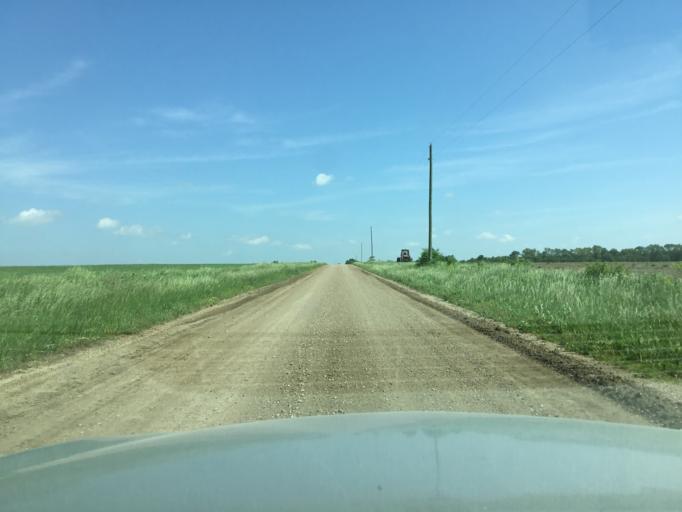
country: US
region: Kansas
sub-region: Labette County
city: Oswego
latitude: 37.1795
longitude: -95.1399
